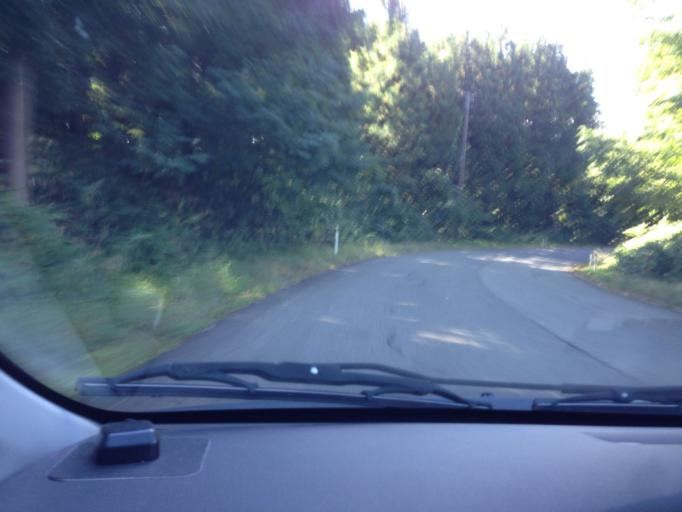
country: JP
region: Fukushima
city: Inawashiro
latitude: 37.5812
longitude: 140.1095
